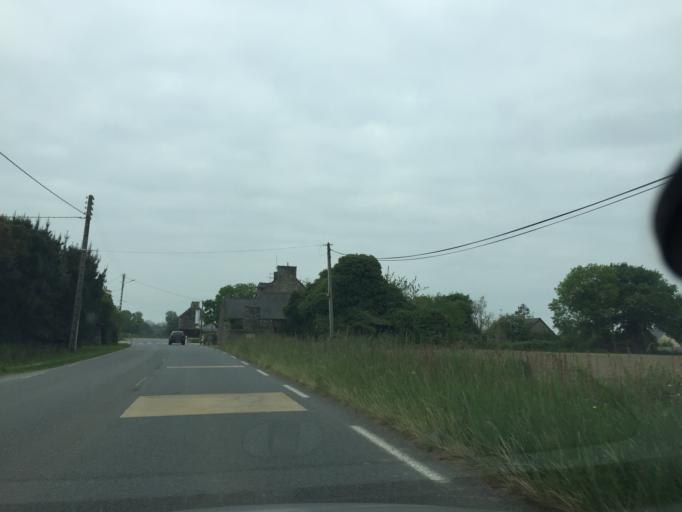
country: FR
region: Brittany
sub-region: Departement des Cotes-d'Armor
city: Matignon
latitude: 48.5941
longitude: -2.2614
